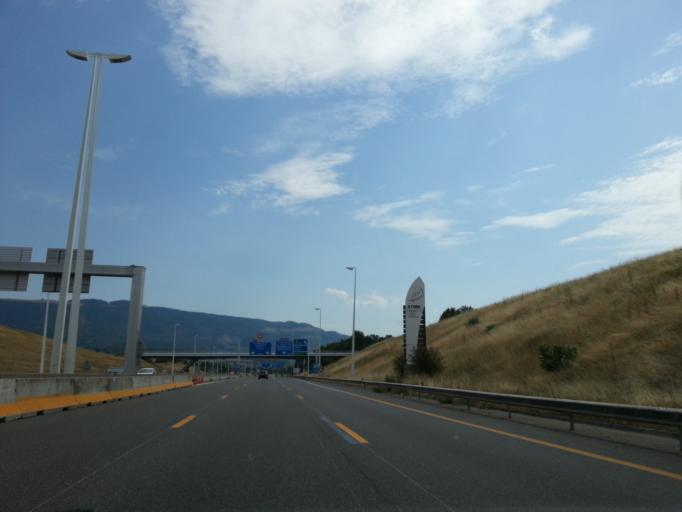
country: FR
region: Rhone-Alpes
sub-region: Departement de la Haute-Savoie
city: Saint-Julien-en-Genevois
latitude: 46.1419
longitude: 6.0979
